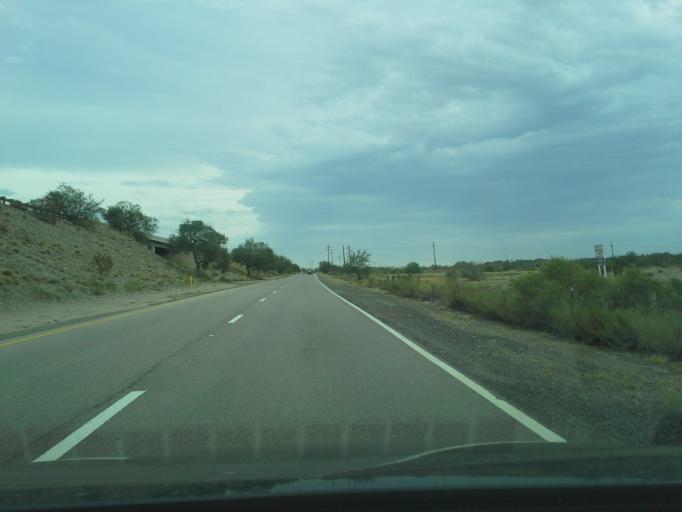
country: US
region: Arizona
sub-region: Pima County
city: Marana
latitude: 32.3978
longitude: -111.1275
